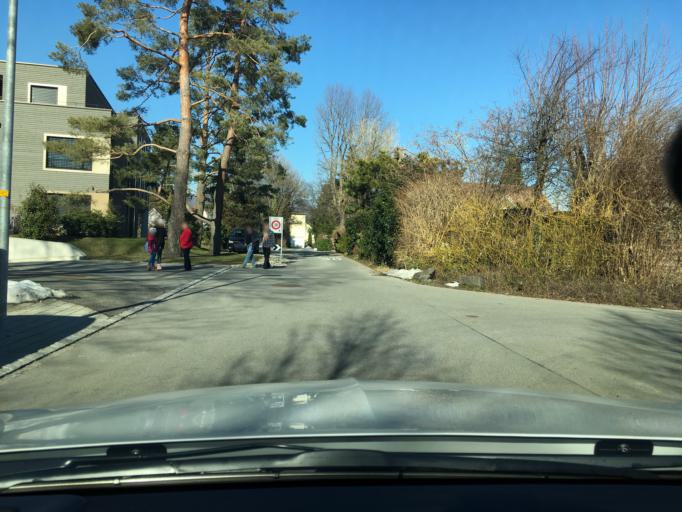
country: CH
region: Appenzell Innerrhoden
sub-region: Appenzell Inner Rhodes
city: Balgach
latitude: 47.4063
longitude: 9.6252
